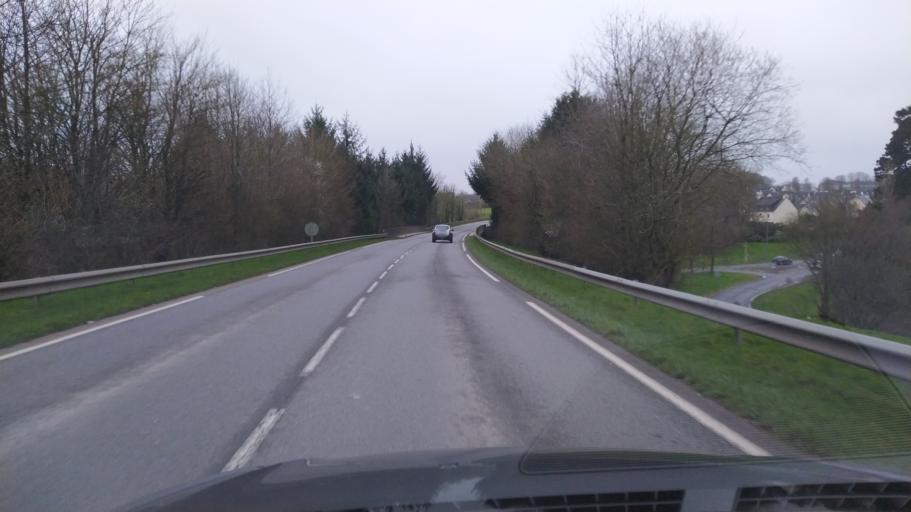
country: FR
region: Brittany
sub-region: Departement du Finistere
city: Landivisiau
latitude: 48.5103
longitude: -4.0536
